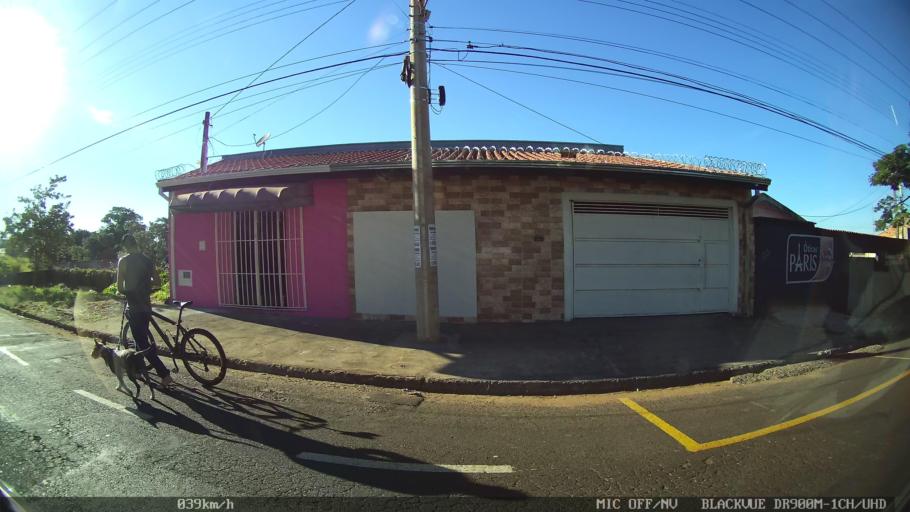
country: BR
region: Sao Paulo
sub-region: Franca
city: Franca
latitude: -20.5758
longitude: -47.3756
